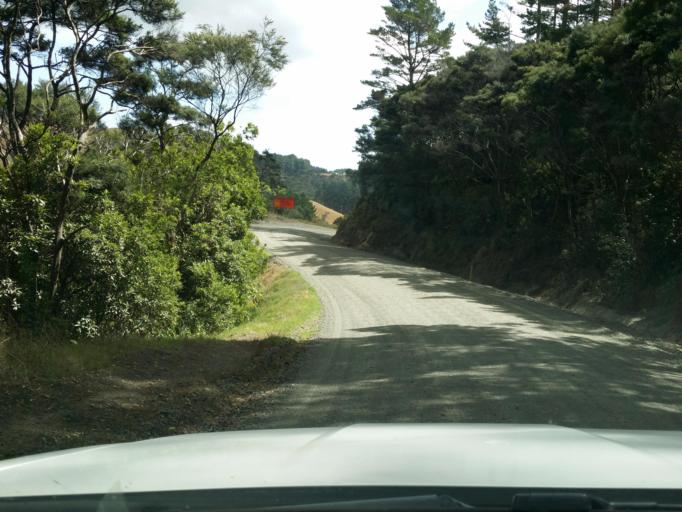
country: NZ
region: Auckland
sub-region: Auckland
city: Wellsford
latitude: -36.3101
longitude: 174.1253
